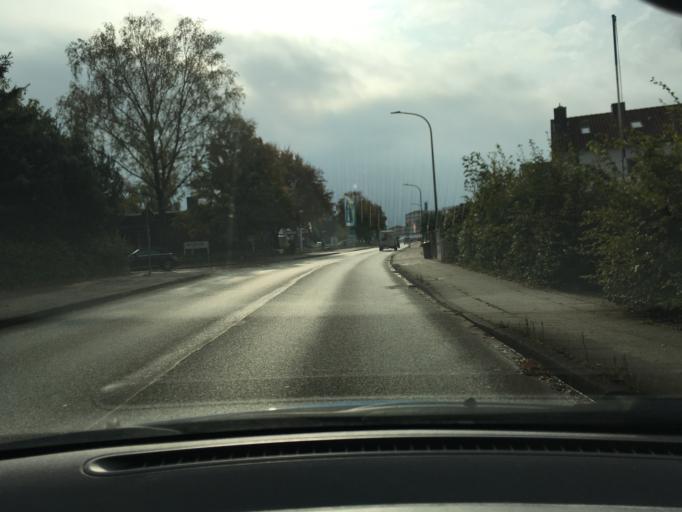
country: DE
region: Schleswig-Holstein
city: Bad Segeberg
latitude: 53.9425
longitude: 10.3002
